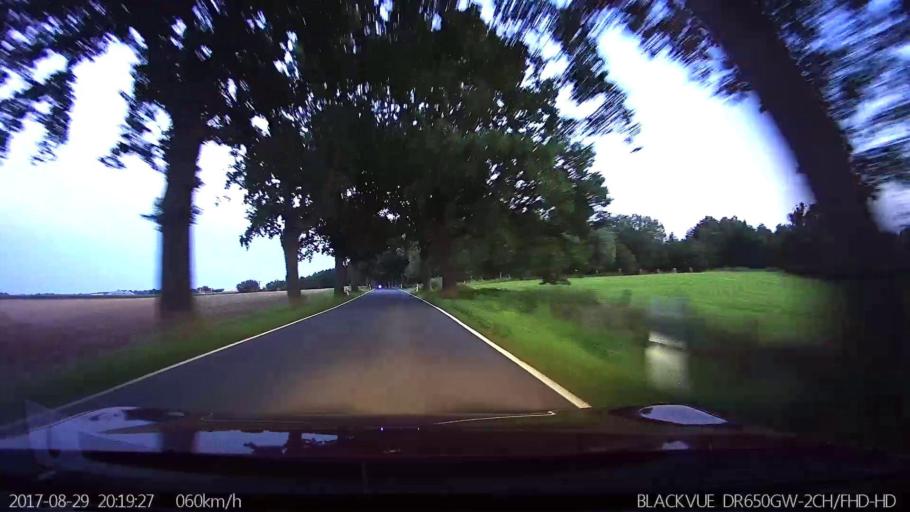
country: DE
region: Mecklenburg-Vorpommern
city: Velgast
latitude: 54.2681
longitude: 12.8129
